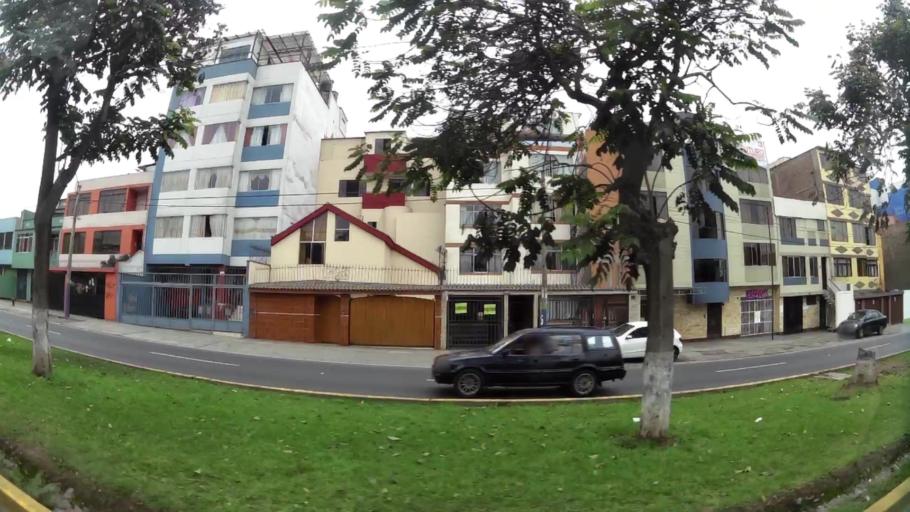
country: PE
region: Lima
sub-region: Lima
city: San Luis
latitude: -12.0768
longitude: -76.9965
